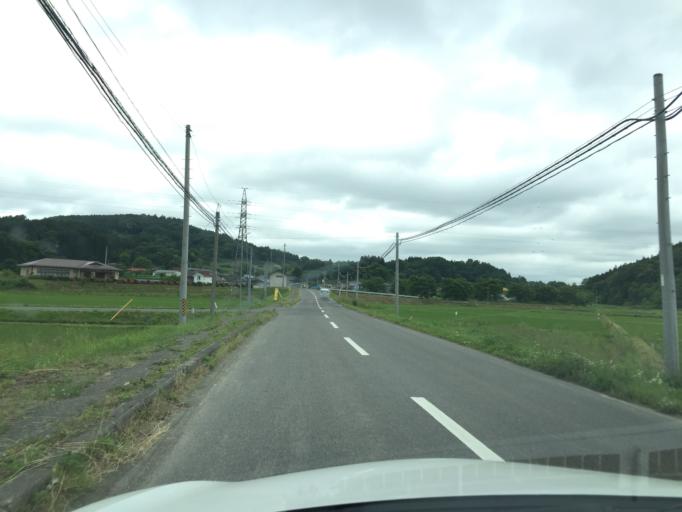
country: JP
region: Fukushima
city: Funehikimachi-funehiki
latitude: 37.4323
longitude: 140.5520
